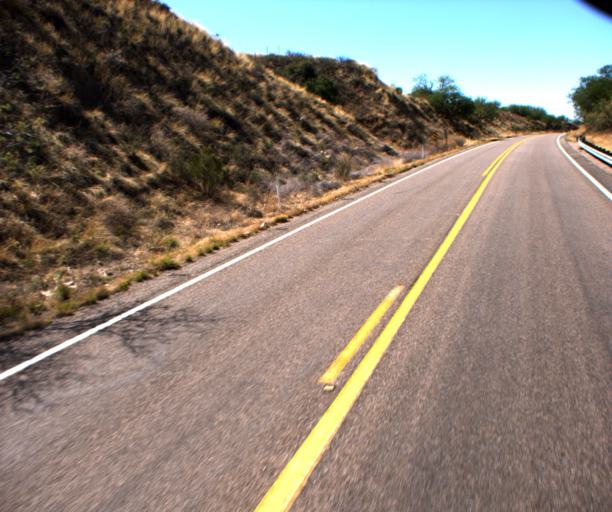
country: US
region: Arizona
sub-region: Santa Cruz County
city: Rio Rico
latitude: 31.4695
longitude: -110.8209
